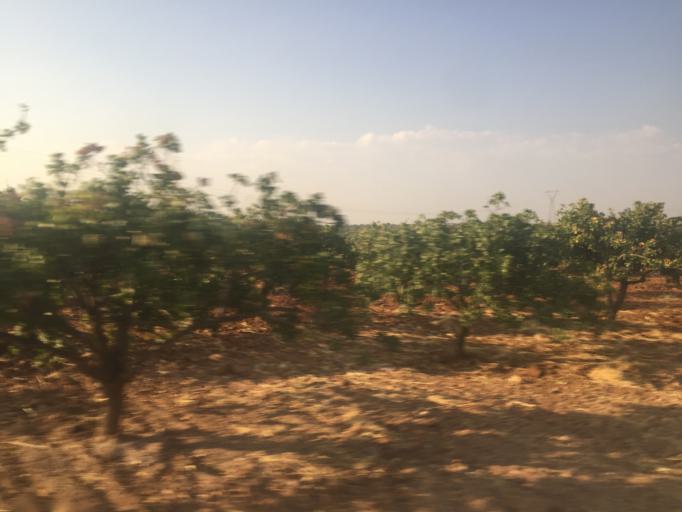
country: TR
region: Gaziantep
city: Nizip
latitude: 37.0142
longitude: 37.8438
